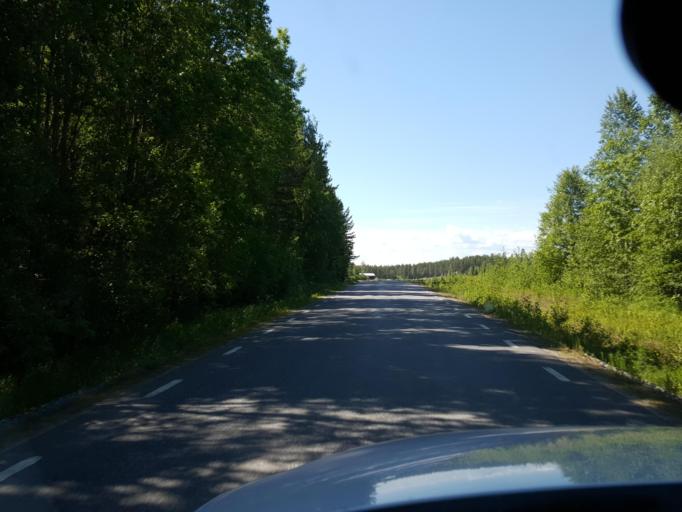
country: SE
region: Gaevleborg
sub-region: Ljusdals Kommun
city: Jaervsoe
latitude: 61.7489
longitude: 16.2521
